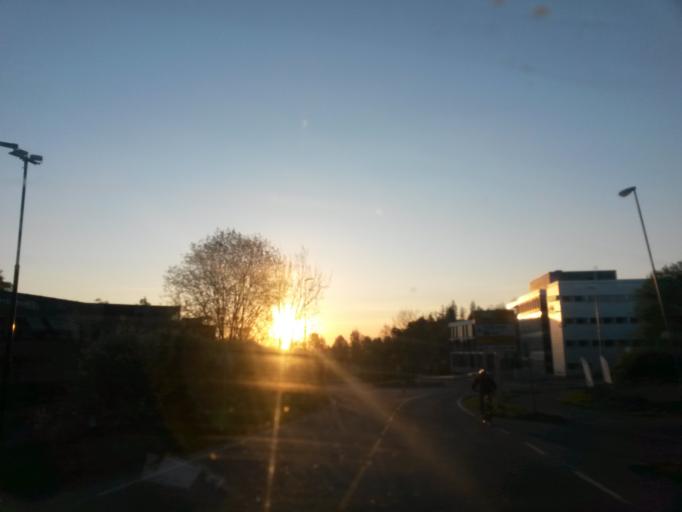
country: NO
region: Akershus
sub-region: Asker
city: Asker
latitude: 59.8299
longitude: 10.4145
